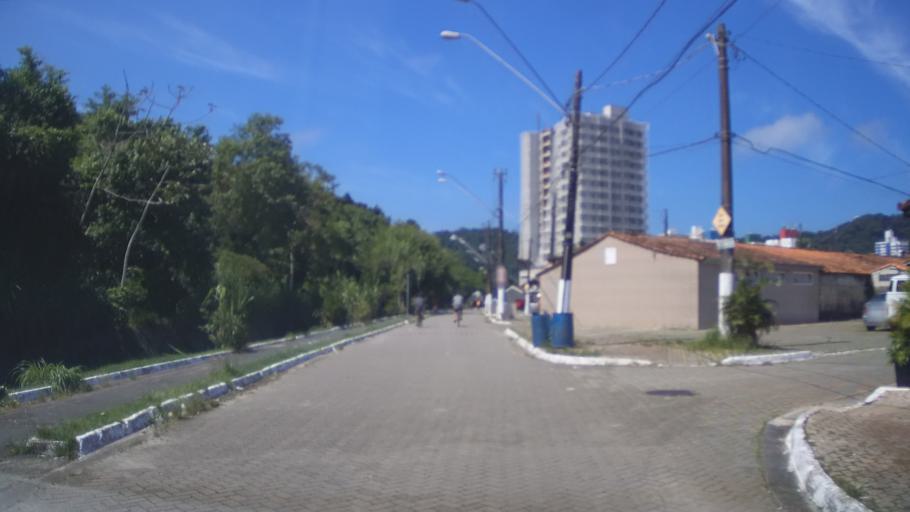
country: BR
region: Sao Paulo
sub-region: Praia Grande
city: Praia Grande
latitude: -24.0059
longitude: -46.3990
